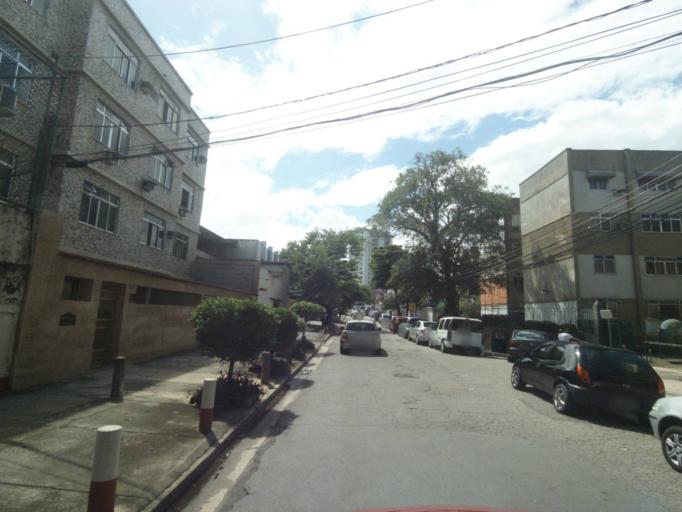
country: BR
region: Rio de Janeiro
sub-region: Sao Joao De Meriti
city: Sao Joao de Meriti
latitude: -22.9266
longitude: -43.3587
